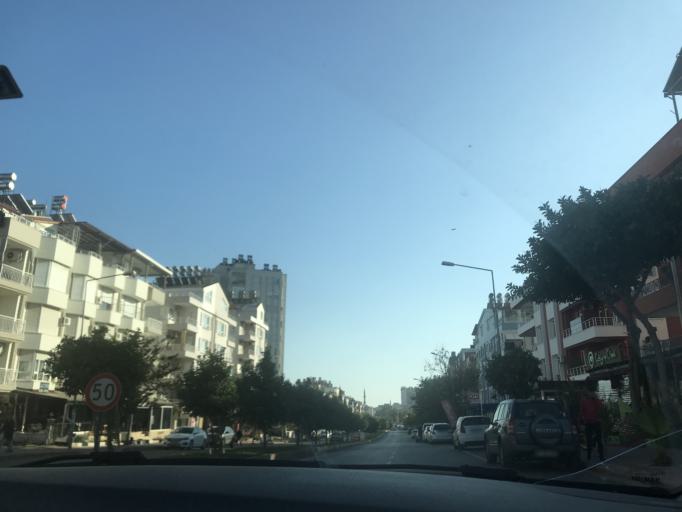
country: TR
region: Antalya
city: Antalya
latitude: 36.8877
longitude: 30.6468
